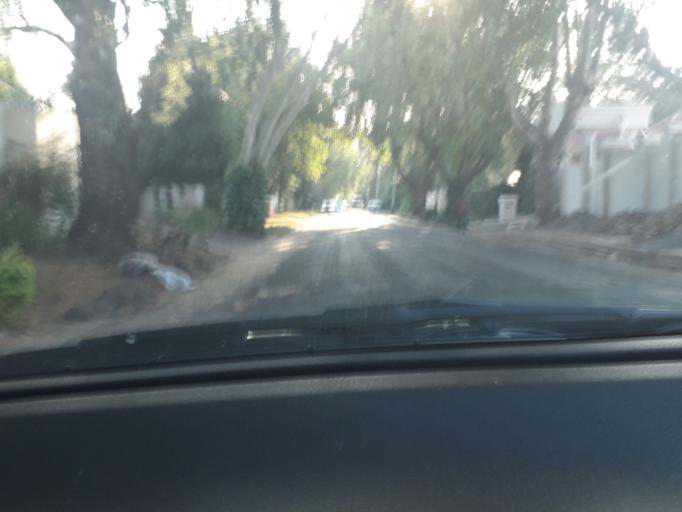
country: ZA
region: Gauteng
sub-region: City of Johannesburg Metropolitan Municipality
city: Johannesburg
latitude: -26.1250
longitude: 28.0762
